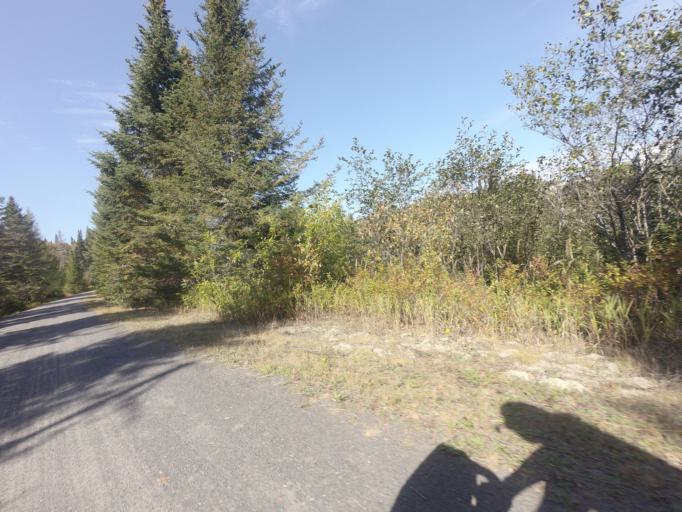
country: CA
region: Quebec
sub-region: Laurentides
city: Sainte-Agathe-des-Monts
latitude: 46.0614
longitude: -74.2995
